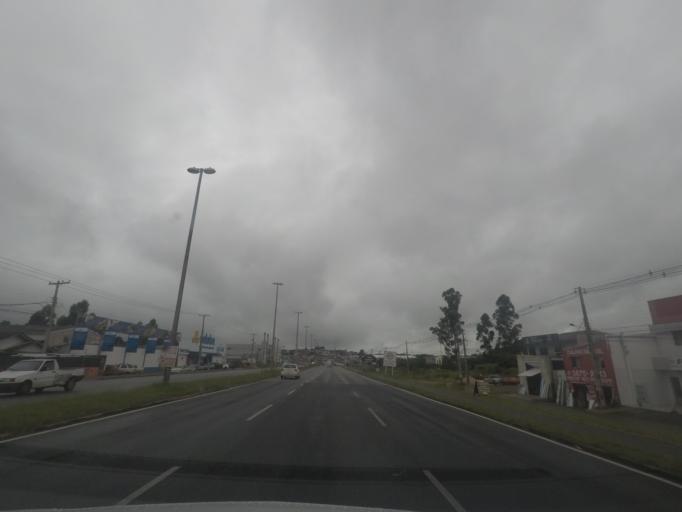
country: BR
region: Parana
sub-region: Colombo
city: Colombo
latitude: -25.3484
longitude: -49.1718
